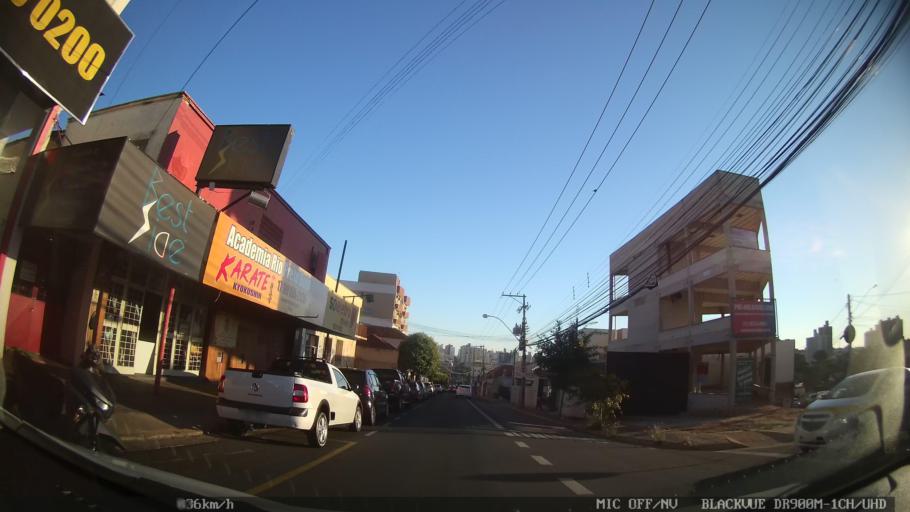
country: BR
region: Sao Paulo
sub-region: Sao Jose Do Rio Preto
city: Sao Jose do Rio Preto
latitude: -20.8047
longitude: -49.3749
